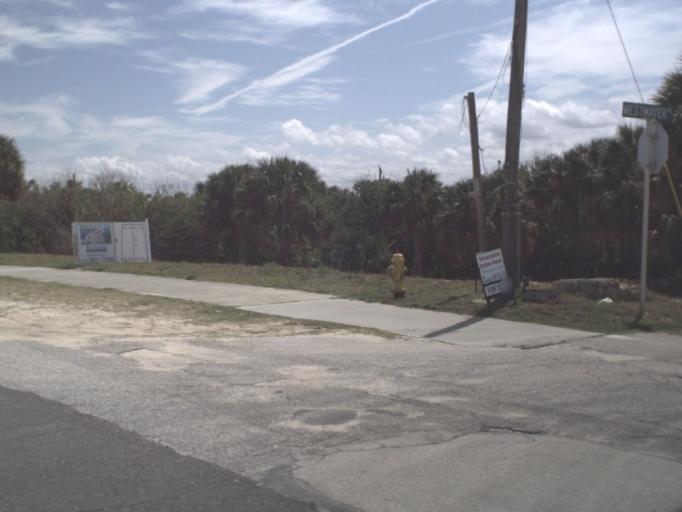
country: US
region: Florida
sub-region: Flagler County
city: Flagler Beach
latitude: 29.5255
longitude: -81.1499
